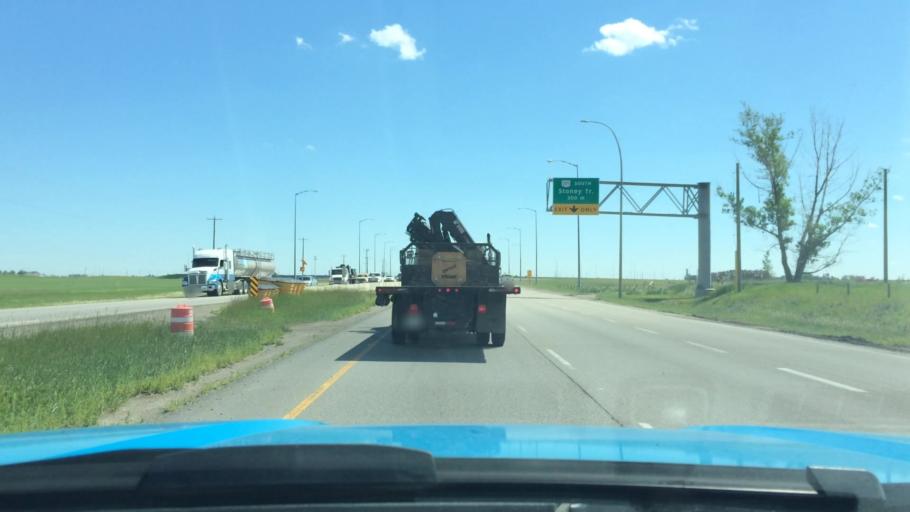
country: CA
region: Alberta
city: Chestermere
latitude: 50.9796
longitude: -113.9331
